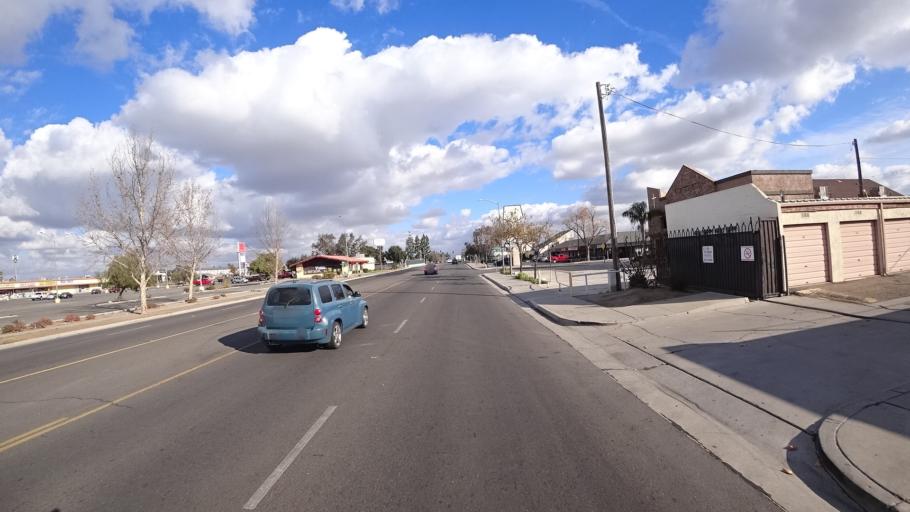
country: US
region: California
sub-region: Kern County
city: Bakersfield
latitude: 35.3322
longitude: -119.0414
